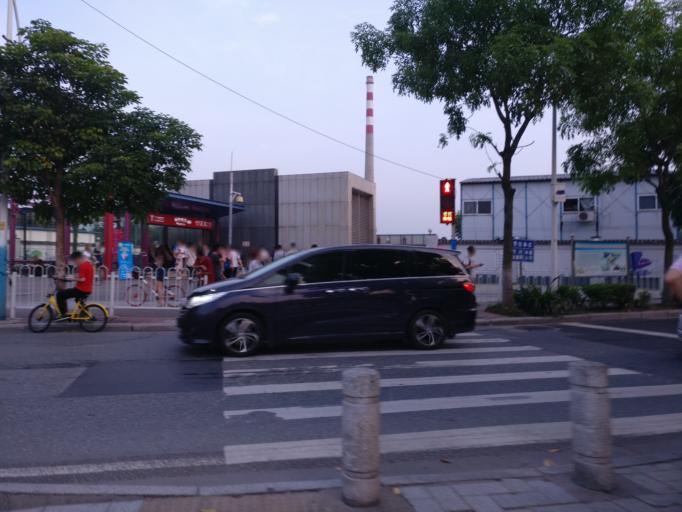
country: CN
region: Guangdong
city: Huangcun
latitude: 23.1218
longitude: 113.3709
